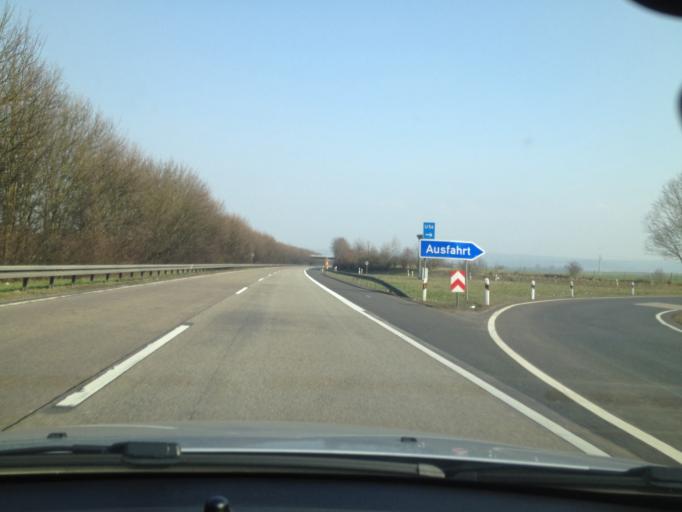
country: DE
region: Hesse
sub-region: Regierungsbezirk Darmstadt
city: Wolfersheim
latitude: 50.4185
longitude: 8.8511
